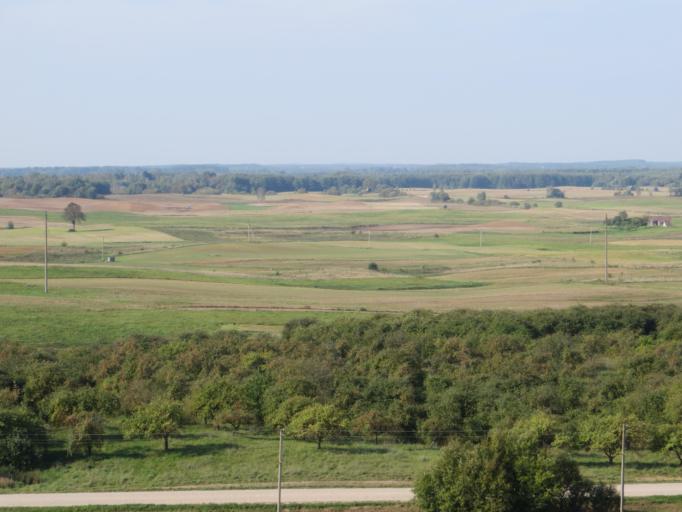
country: LT
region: Alytaus apskritis
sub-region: Alytaus rajonas
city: Daugai
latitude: 54.3271
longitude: 24.4526
